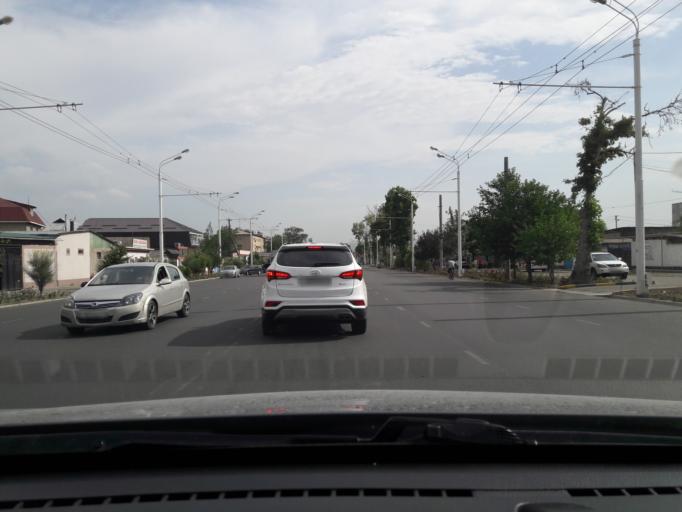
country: TJ
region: Dushanbe
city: Dushanbe
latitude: 38.5382
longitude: 68.7543
